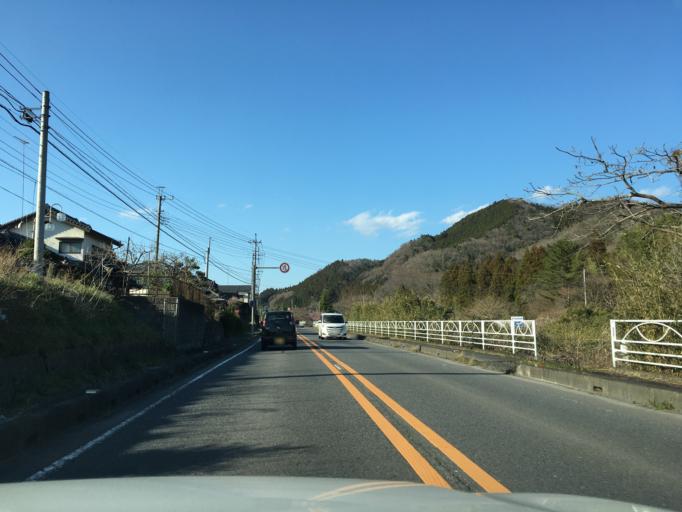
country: JP
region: Ibaraki
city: Omiya
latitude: 36.6522
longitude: 140.3935
